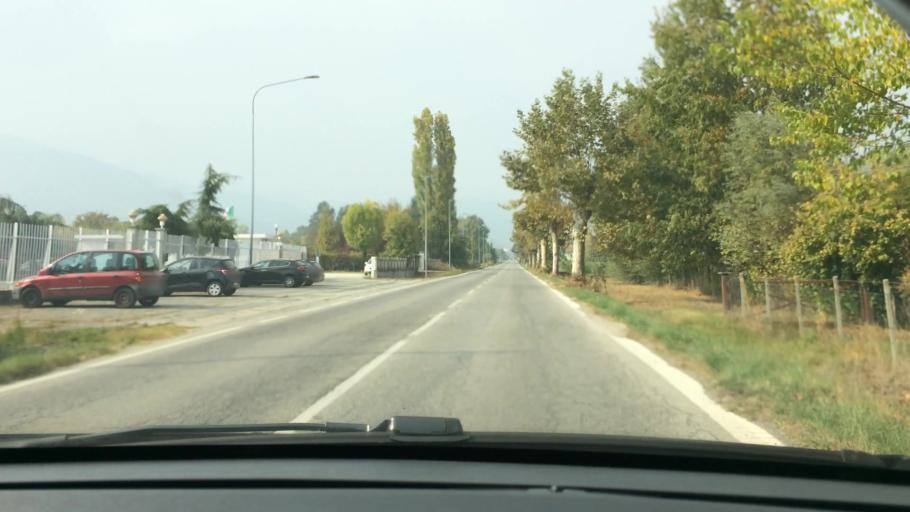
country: IT
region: Piedmont
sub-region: Provincia di Torino
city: Cumiana
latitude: 44.9615
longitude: 7.4014
